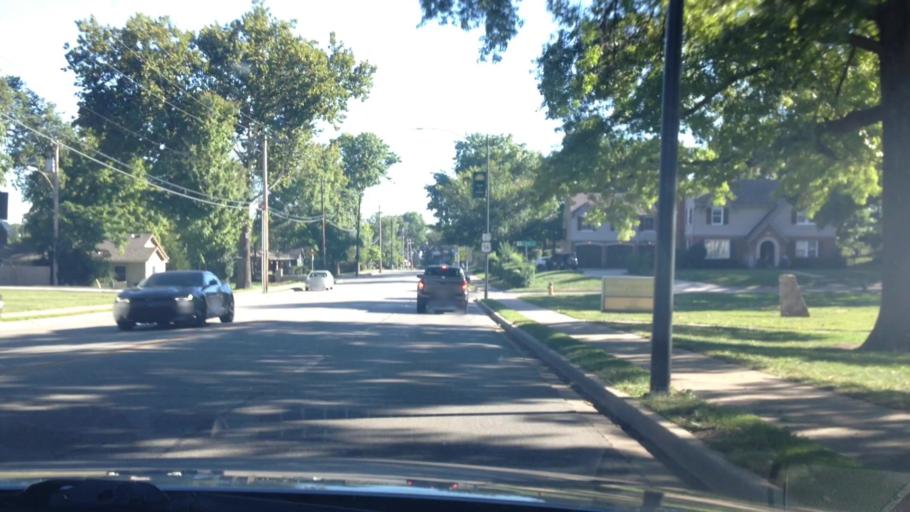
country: US
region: Kansas
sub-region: Johnson County
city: Westwood
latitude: 39.0366
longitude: -94.6120
